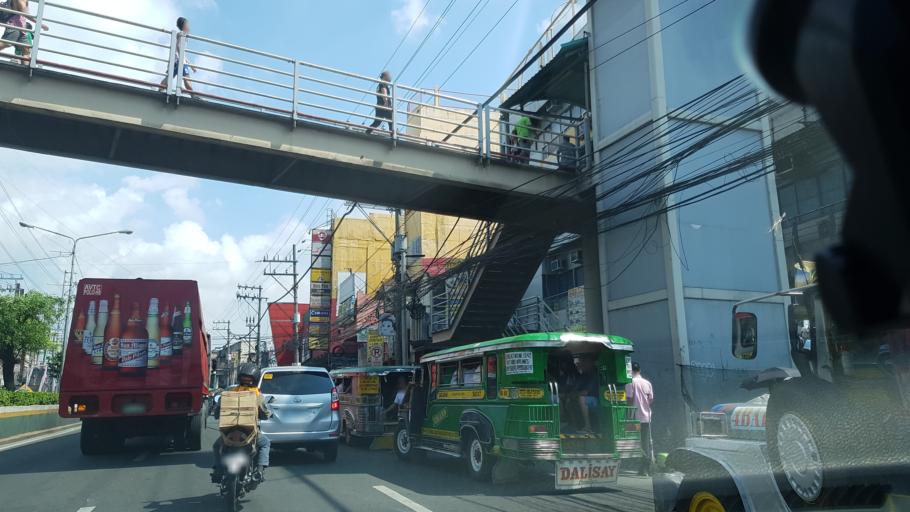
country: PH
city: Sambayanihan People's Village
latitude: 14.4758
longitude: 121.0003
